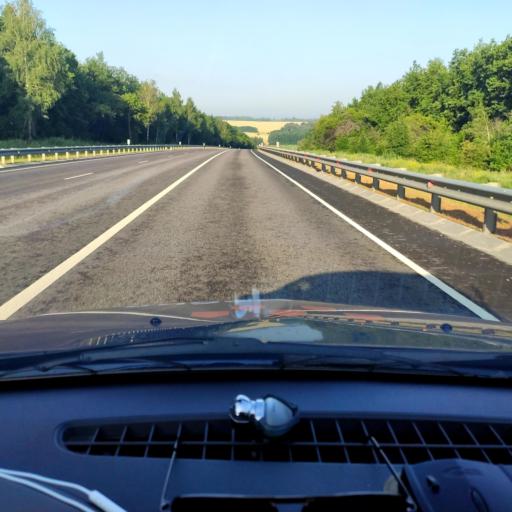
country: RU
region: Lipetsk
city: Izmalkovo
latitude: 52.4443
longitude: 37.9689
